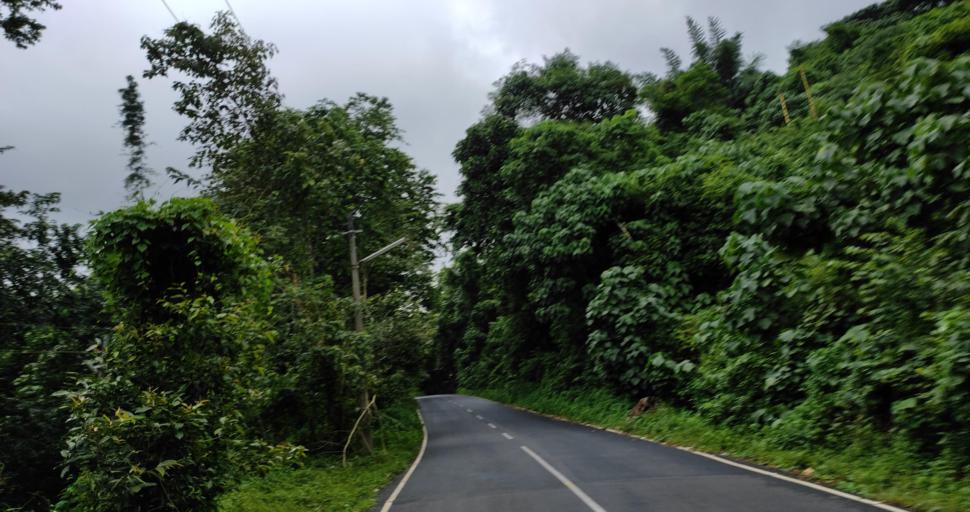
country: IN
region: Kerala
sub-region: Ernakulam
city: Angamali
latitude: 10.2982
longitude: 76.4577
